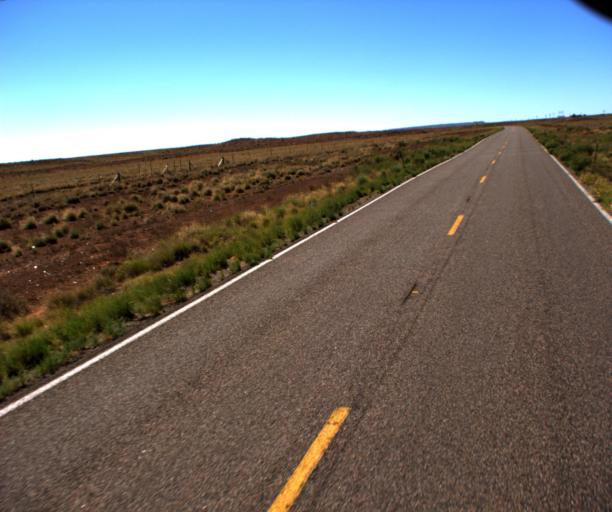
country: US
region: Arizona
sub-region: Coconino County
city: LeChee
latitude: 35.1657
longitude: -110.9137
